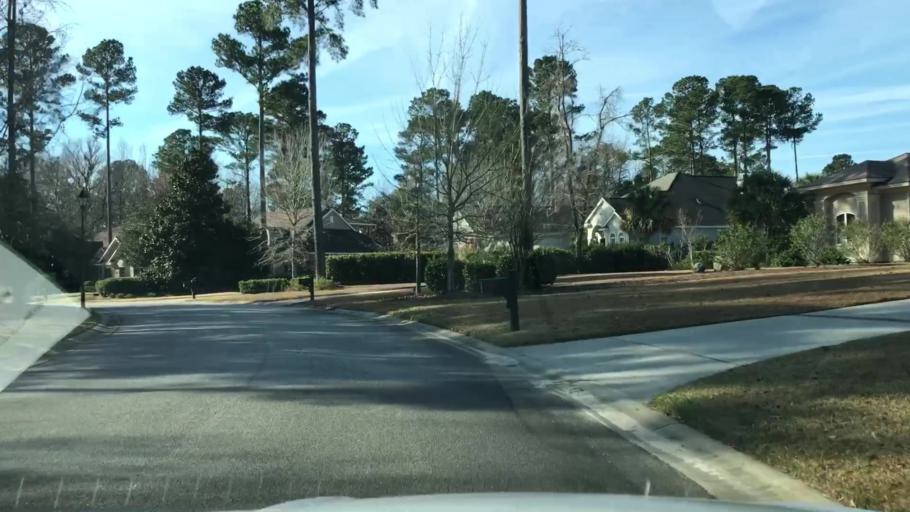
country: US
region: South Carolina
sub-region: Beaufort County
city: Bluffton
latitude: 32.2455
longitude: -80.9133
